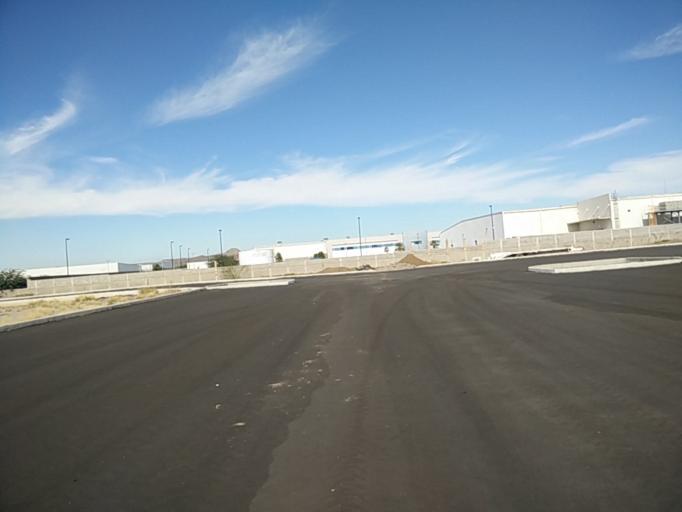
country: MX
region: Sonora
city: Hermosillo
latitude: 29.0962
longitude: -111.0245
